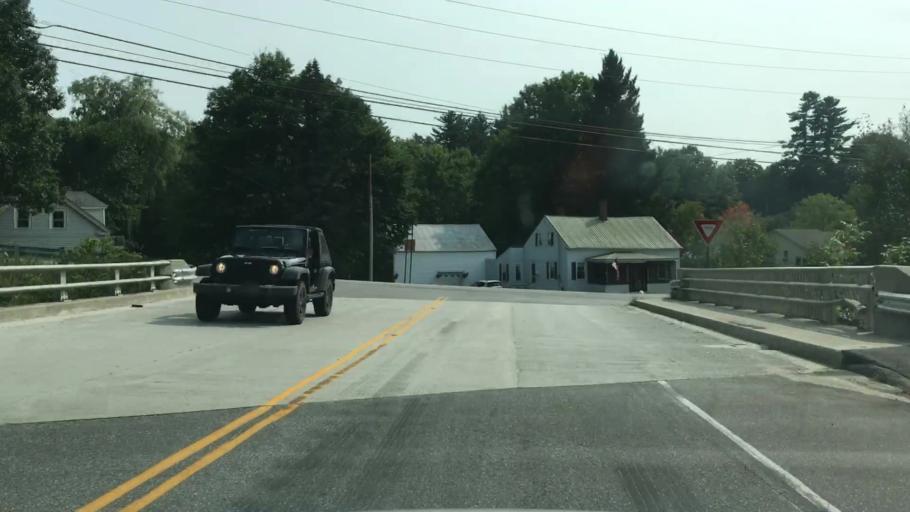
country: US
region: Maine
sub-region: Oxford County
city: South Paris
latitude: 44.2225
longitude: -70.5061
